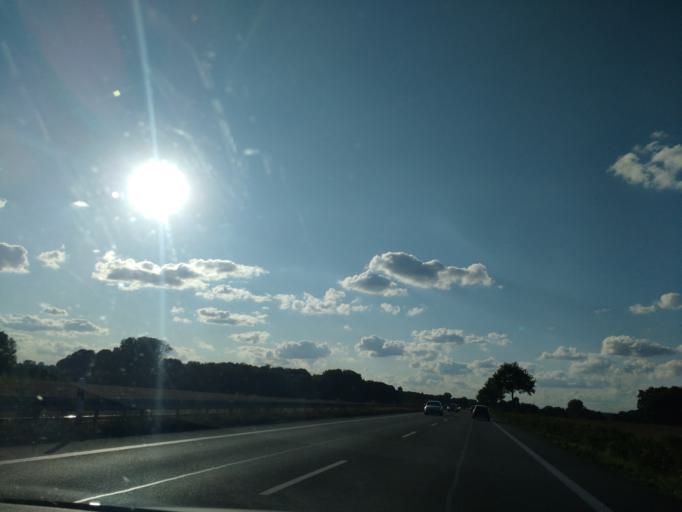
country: DE
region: North Rhine-Westphalia
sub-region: Regierungsbezirk Munster
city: Beelen
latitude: 51.9390
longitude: 8.0800
